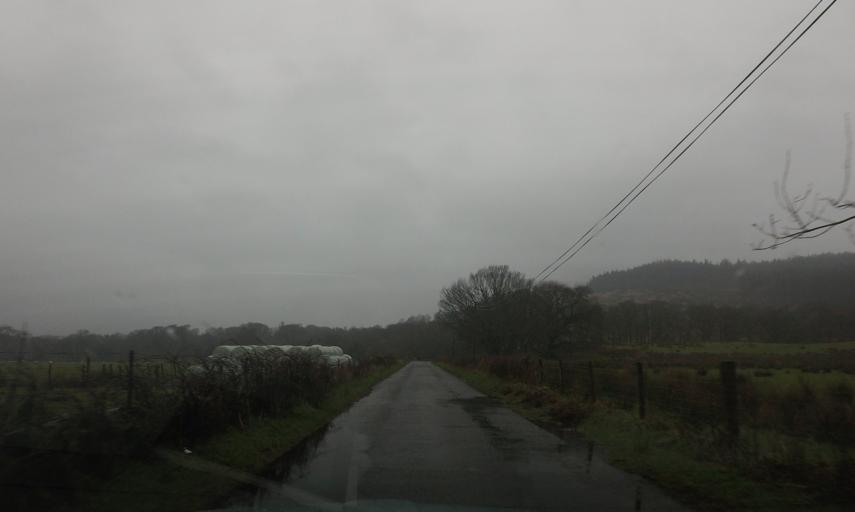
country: GB
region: Scotland
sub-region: West Dunbartonshire
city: Balloch
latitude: 56.1399
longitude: -4.6199
